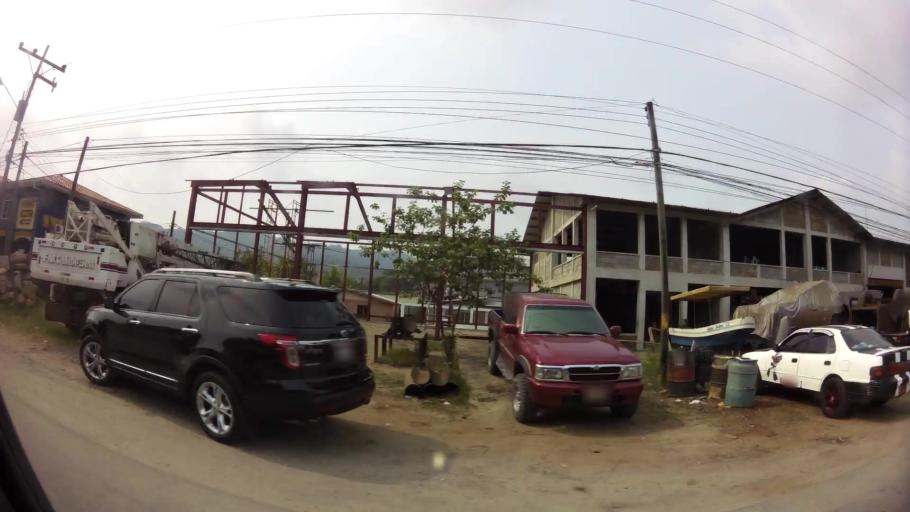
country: HN
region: Atlantida
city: Tela
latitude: 15.7632
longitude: -87.4766
